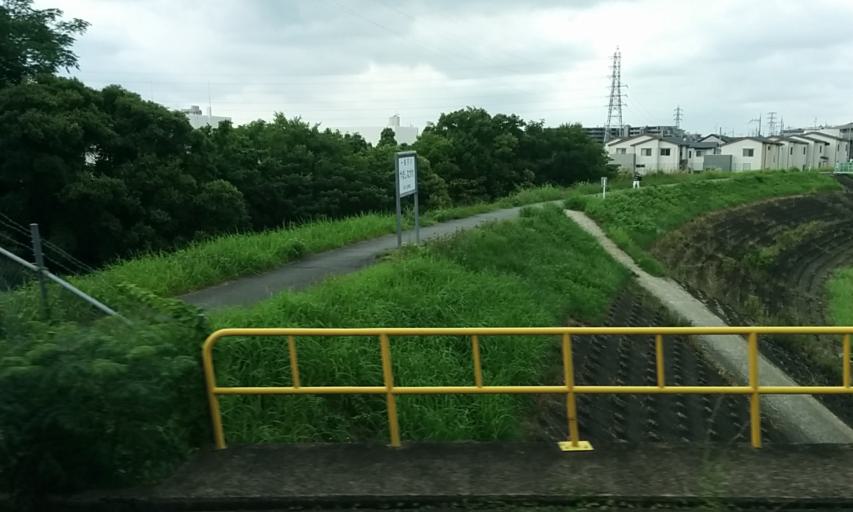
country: JP
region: Kyoto
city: Uji
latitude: 34.9315
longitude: 135.7943
